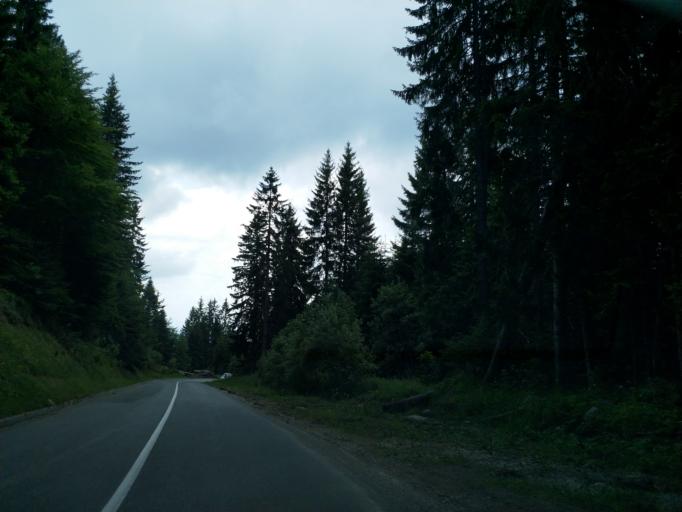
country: XK
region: Mitrovica
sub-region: Komuna e Leposaviqit
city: Leposaviq
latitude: 43.2758
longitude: 20.7917
